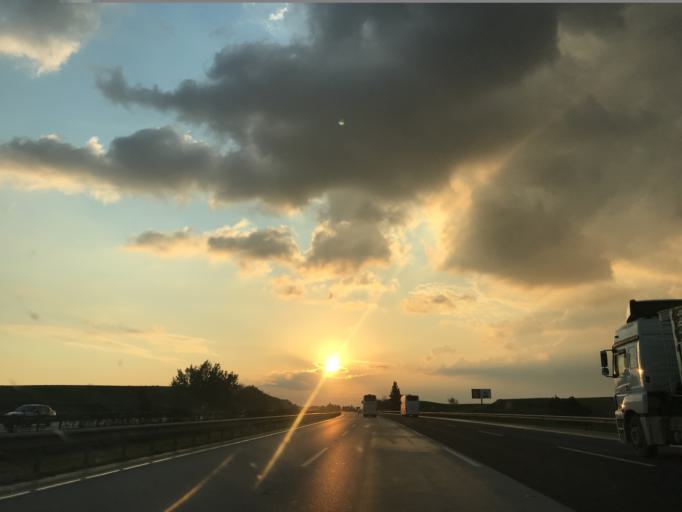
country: TR
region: Mersin
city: Yenice
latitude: 37.0397
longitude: 35.1521
